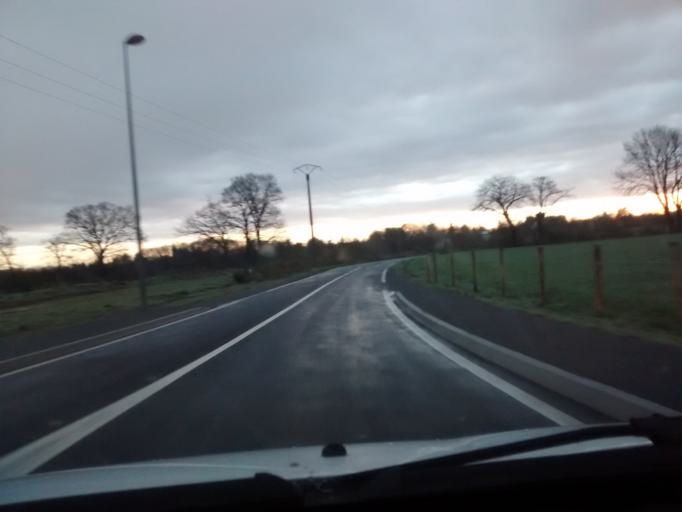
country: FR
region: Brittany
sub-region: Departement d'Ille-et-Vilaine
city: Chateaubourg
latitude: 48.0993
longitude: -1.4007
